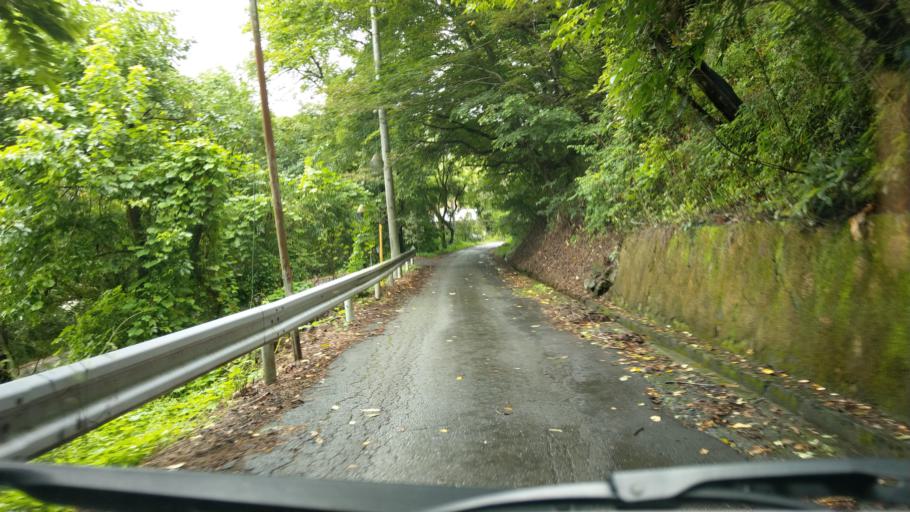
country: JP
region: Nagano
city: Komoro
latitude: 36.3027
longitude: 138.4204
